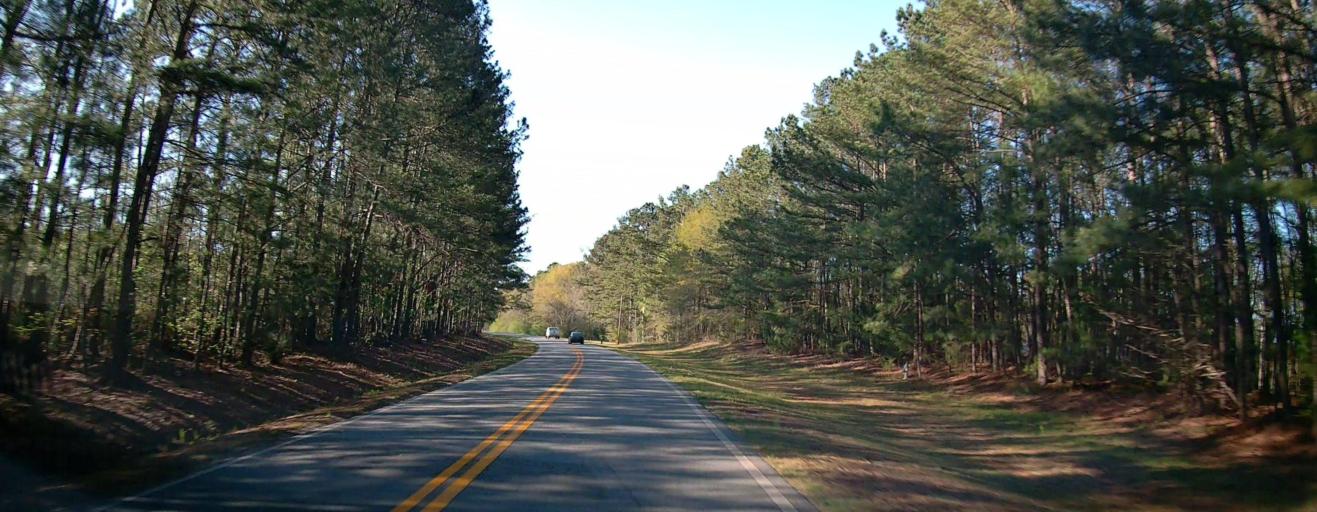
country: US
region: Georgia
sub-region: Butts County
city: Jackson
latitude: 33.3238
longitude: -83.9022
